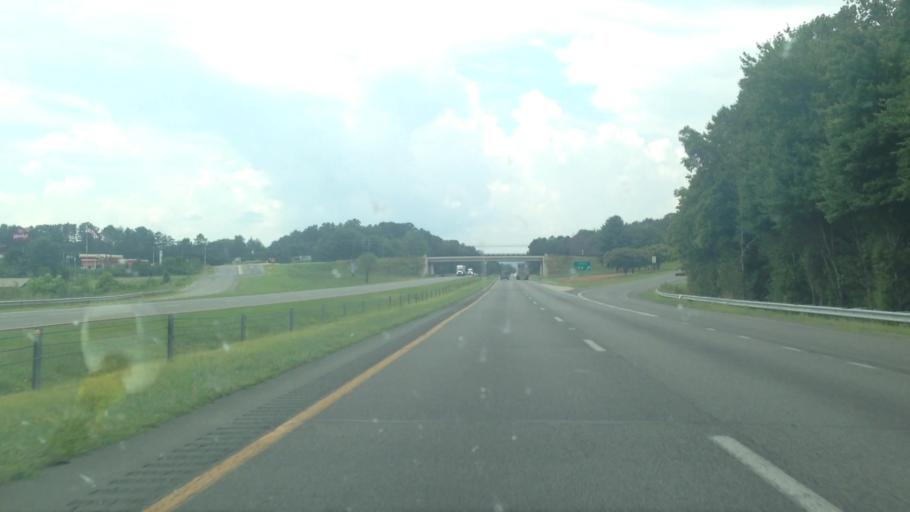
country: US
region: North Carolina
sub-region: Surry County
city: Pilot Mountain
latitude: 36.3730
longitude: -80.4852
